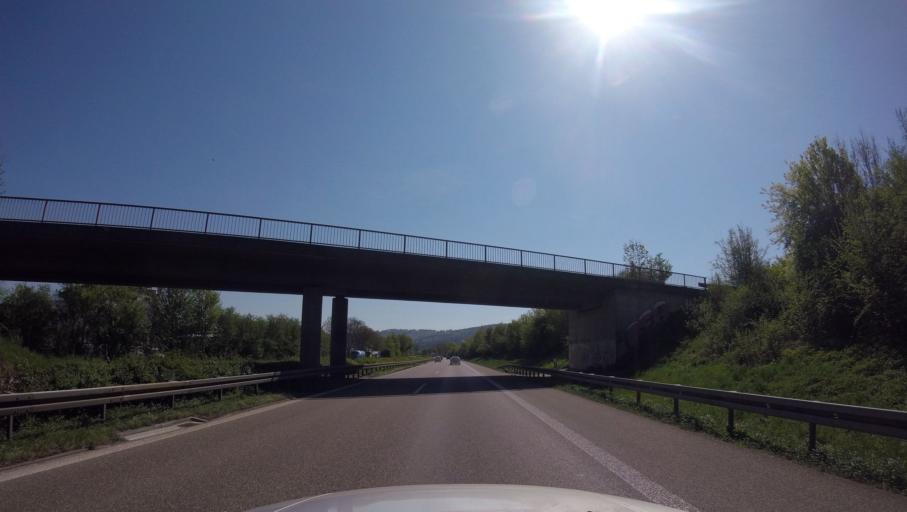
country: DE
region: Baden-Wuerttemberg
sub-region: Regierungsbezirk Stuttgart
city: Pluderhausen
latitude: 48.7855
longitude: 9.6037
